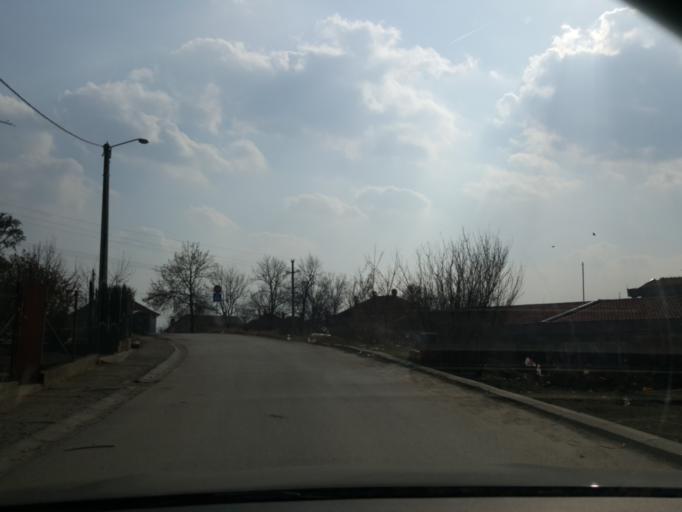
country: RS
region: Central Serbia
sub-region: Nisavski Okrug
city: Aleksinac
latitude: 43.5357
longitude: 21.7174
